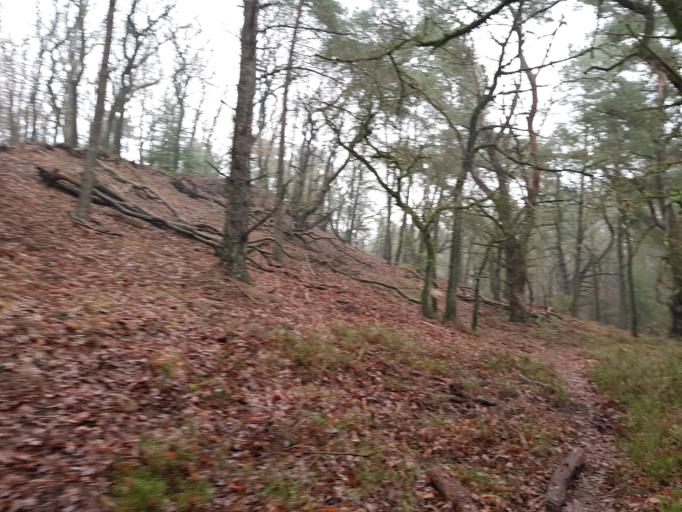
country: NL
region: Gelderland
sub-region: Gemeente Apeldoorn
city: Loenen
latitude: 52.1007
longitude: 5.9720
